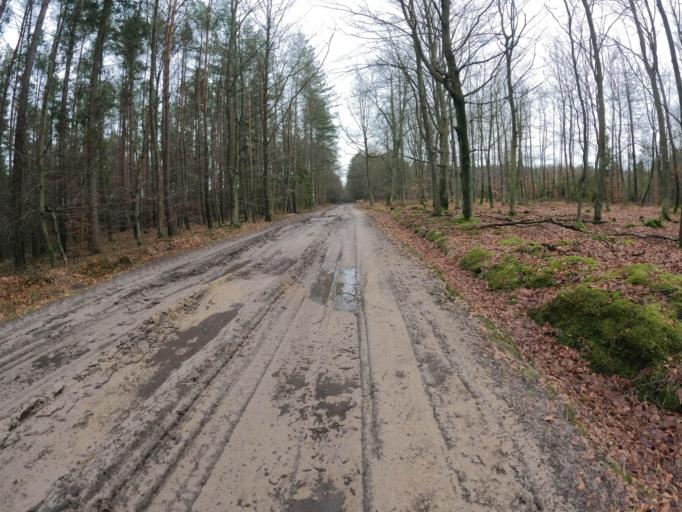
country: PL
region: West Pomeranian Voivodeship
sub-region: Powiat slawienski
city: Darlowo
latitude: 54.3923
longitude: 16.4847
